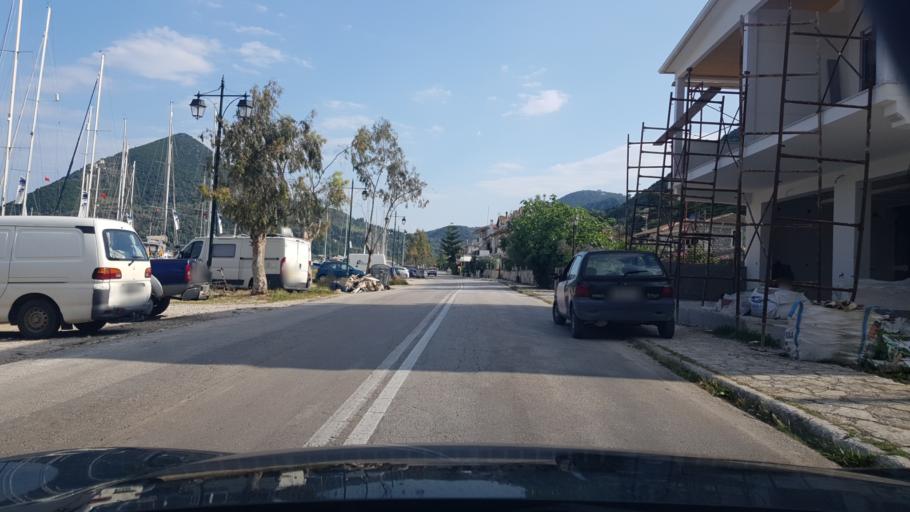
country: GR
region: Ionian Islands
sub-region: Lefkada
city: Nidri
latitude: 38.6871
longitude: 20.6986
